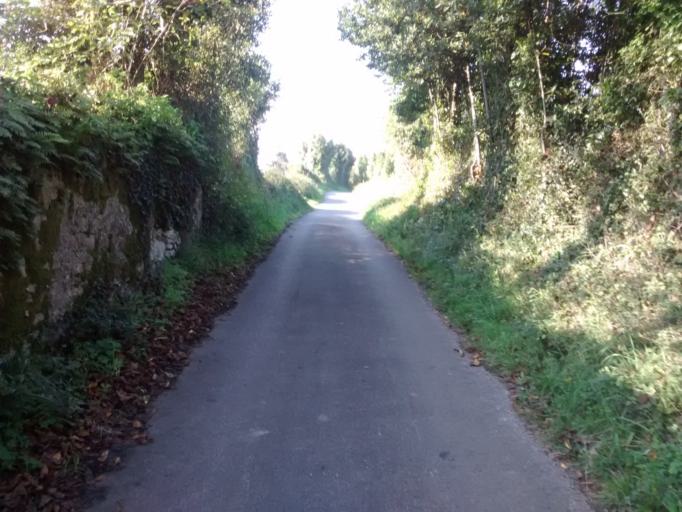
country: ES
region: Asturias
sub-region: Province of Asturias
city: Colunga
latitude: 43.4676
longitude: -5.2327
